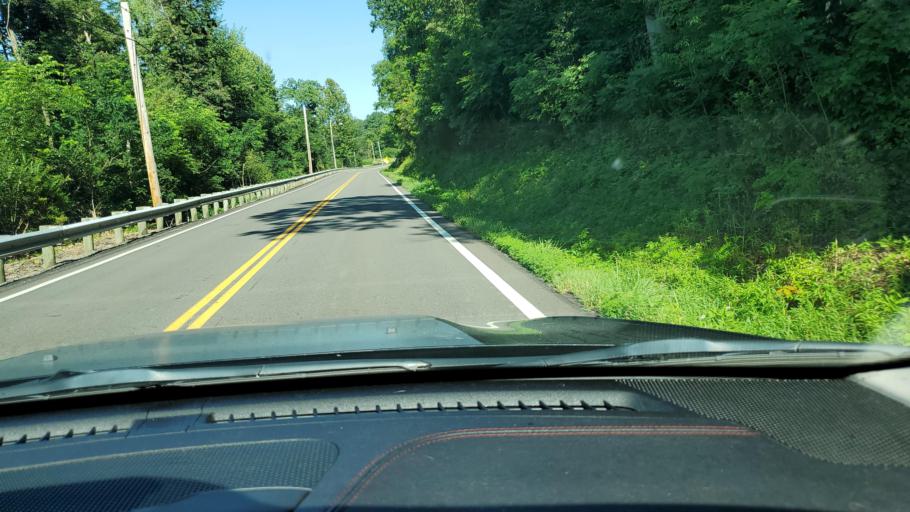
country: US
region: Ohio
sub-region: Mahoning County
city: Lowellville
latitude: 41.0461
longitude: -80.5530
